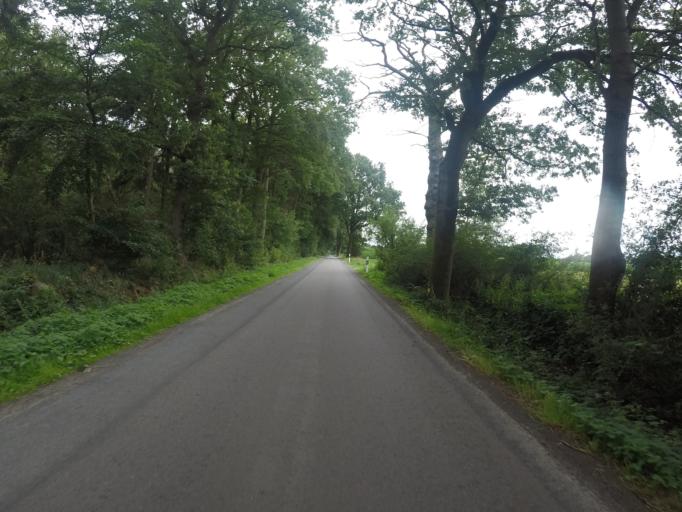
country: DE
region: Lower Saxony
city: Himmelpforten
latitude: 53.6089
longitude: 9.3234
